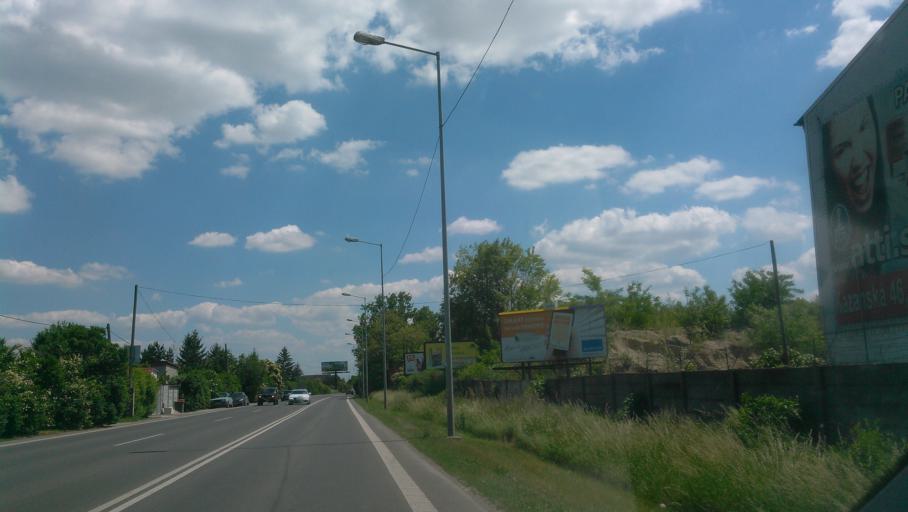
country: SK
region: Bratislavsky
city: Dunajska Luzna
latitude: 48.1206
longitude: 17.2084
